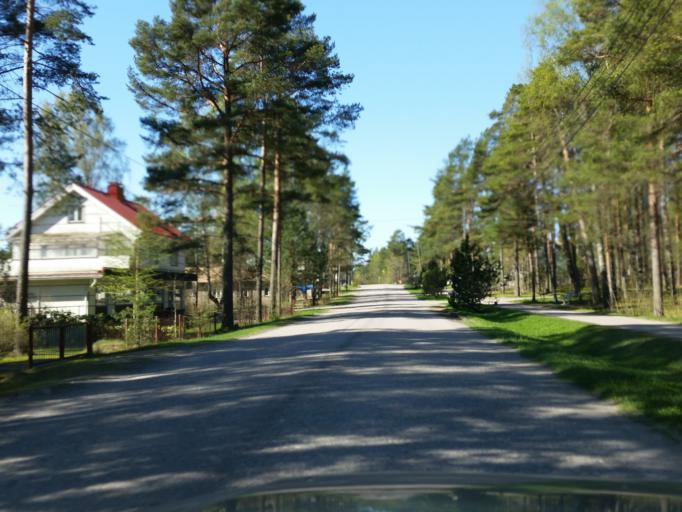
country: FI
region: Uusimaa
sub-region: Raaseporin
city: Inga
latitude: 60.1388
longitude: 23.8678
